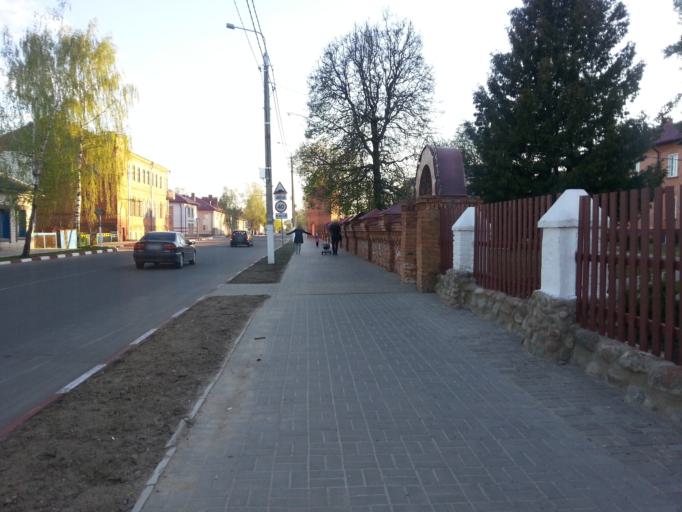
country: BY
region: Mogilev
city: Mstsislaw
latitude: 54.0219
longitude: 31.7322
